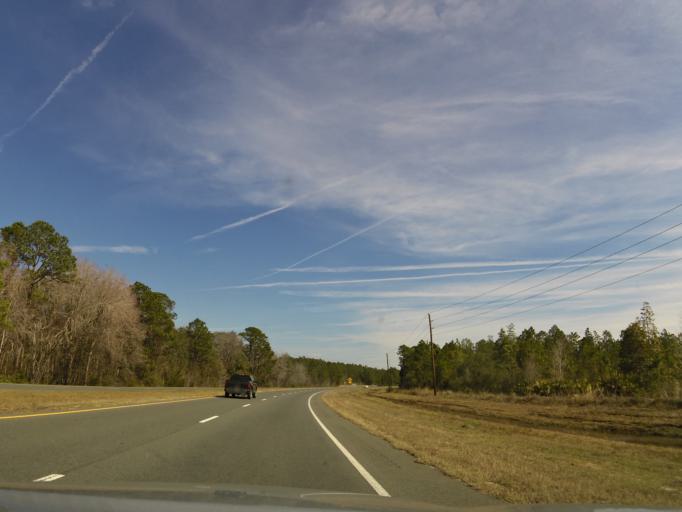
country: US
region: Georgia
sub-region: Brantley County
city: Nahunta
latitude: 31.1852
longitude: -82.1054
